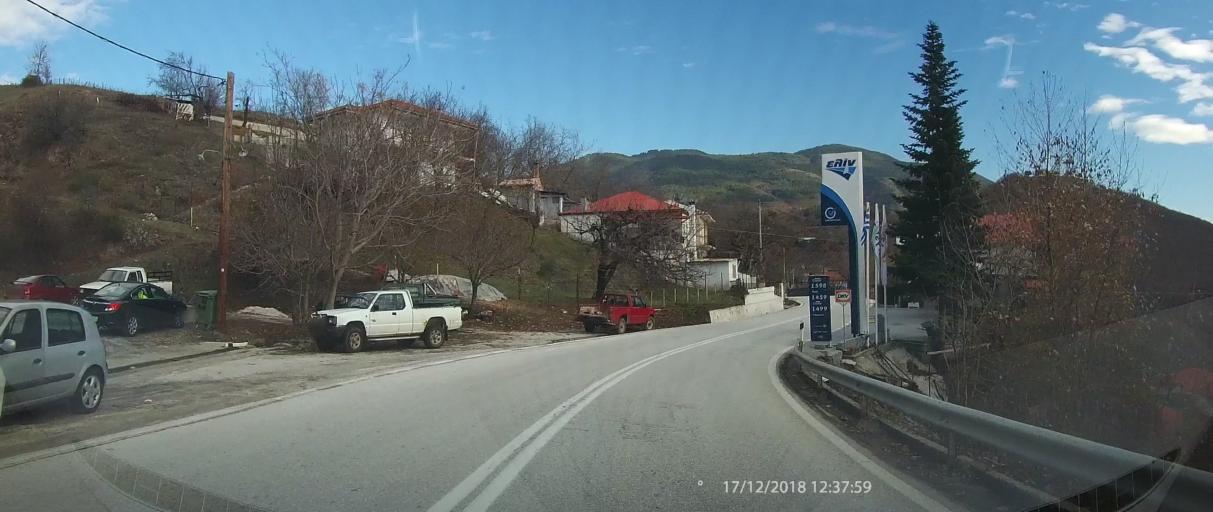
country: GR
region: Epirus
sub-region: Nomos Ioanninon
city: Metsovo
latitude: 39.8092
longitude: 21.3424
